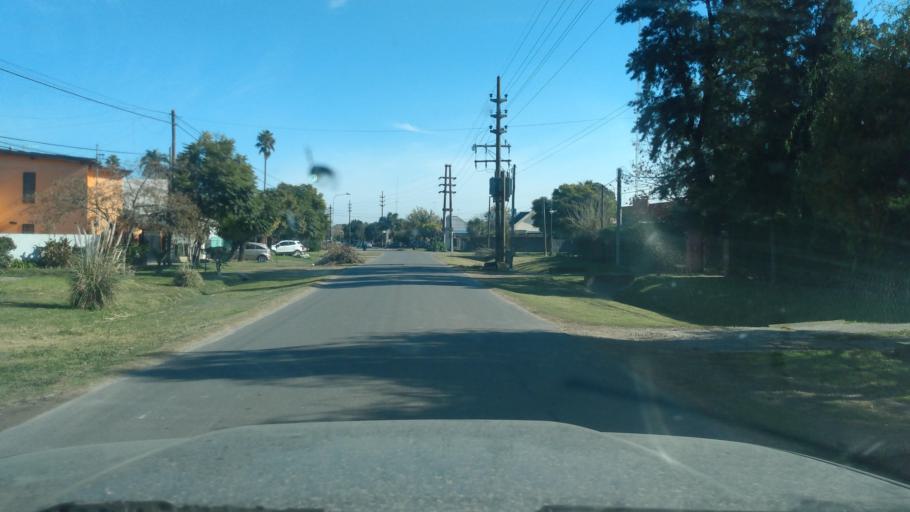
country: AR
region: Buenos Aires
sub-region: Partido de Lujan
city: Lujan
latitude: -34.5782
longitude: -59.1007
